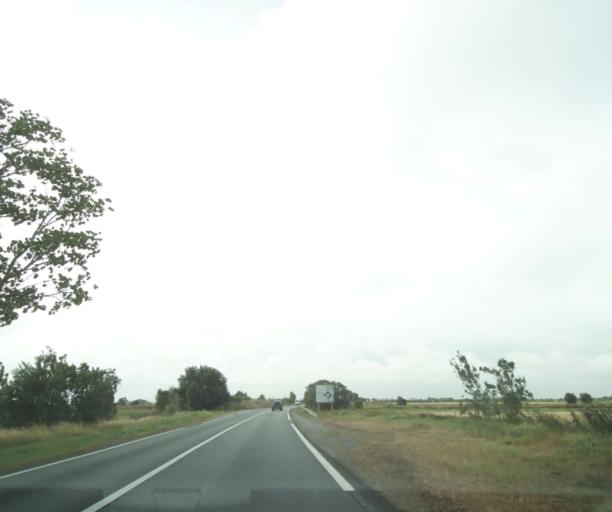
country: FR
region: Poitou-Charentes
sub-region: Departement de la Charente-Maritime
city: Andilly
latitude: 46.2556
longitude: -1.0664
